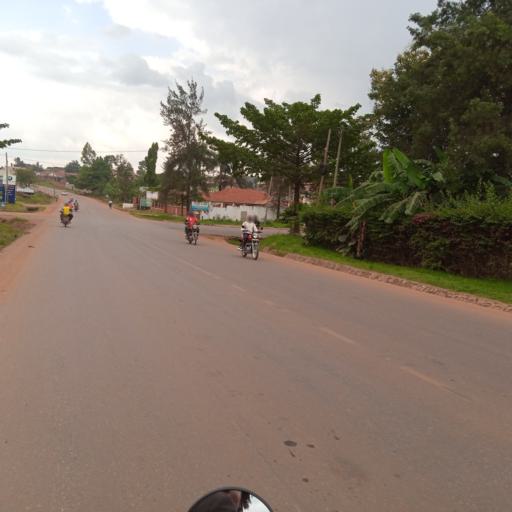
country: UG
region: Eastern Region
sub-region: Mbale District
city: Mbale
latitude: 1.0740
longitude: 34.1710
